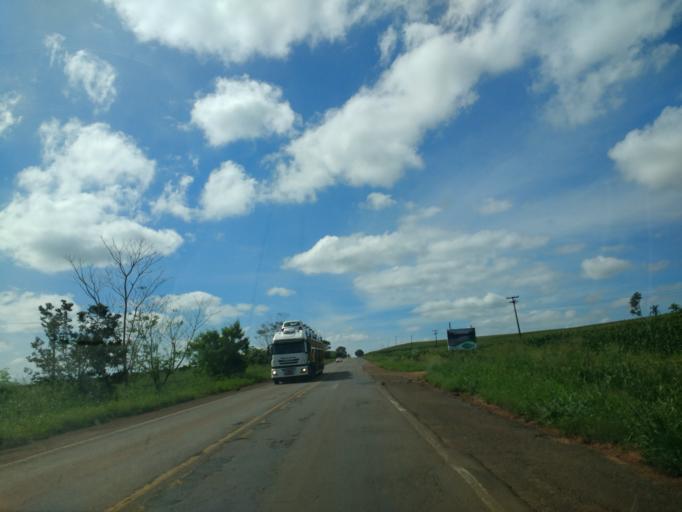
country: BR
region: Parana
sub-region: Terra Boa
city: Terra Boa
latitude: -23.6141
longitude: -52.4283
